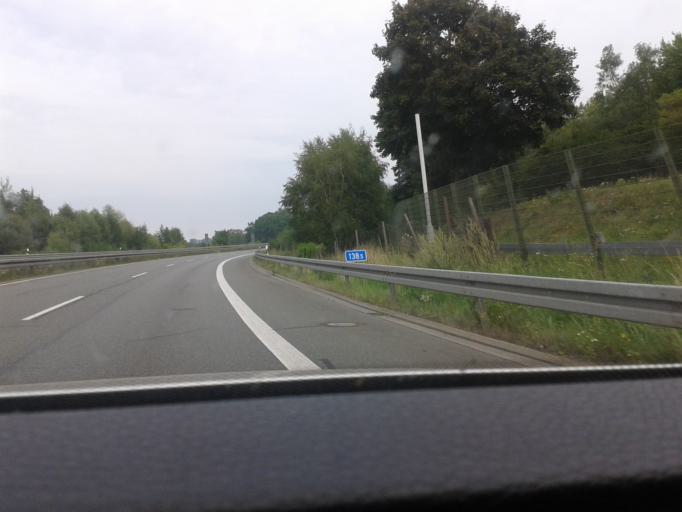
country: DE
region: Lower Saxony
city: Weyhausen
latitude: 52.4445
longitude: 10.7348
